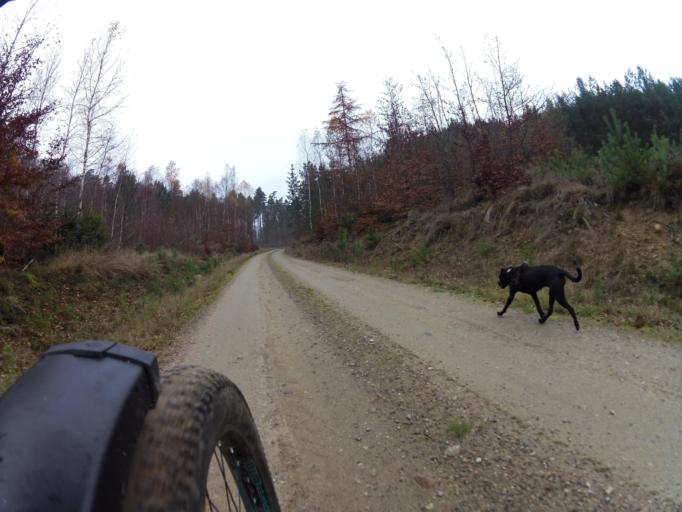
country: PL
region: Pomeranian Voivodeship
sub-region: Powiat pucki
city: Krokowa
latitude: 54.7093
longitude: 18.1457
